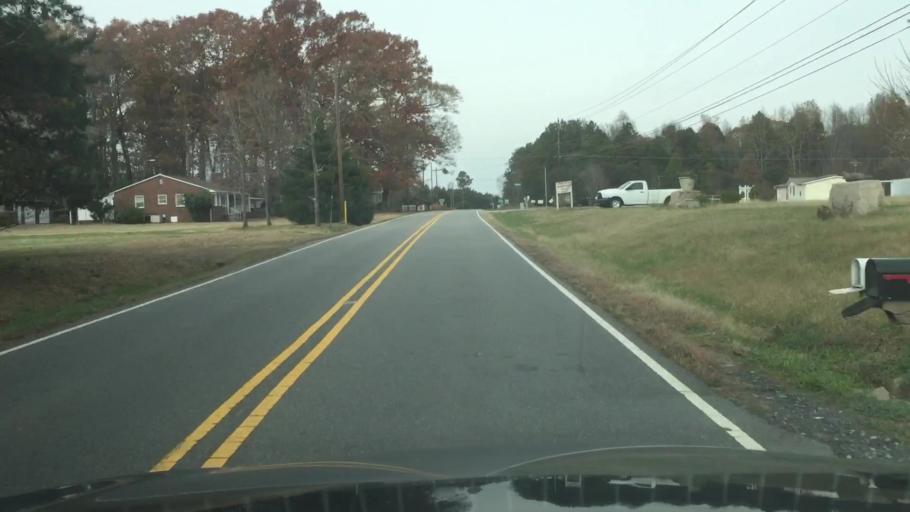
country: US
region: North Carolina
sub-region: Iredell County
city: Mooresville
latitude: 35.6069
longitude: -80.7555
